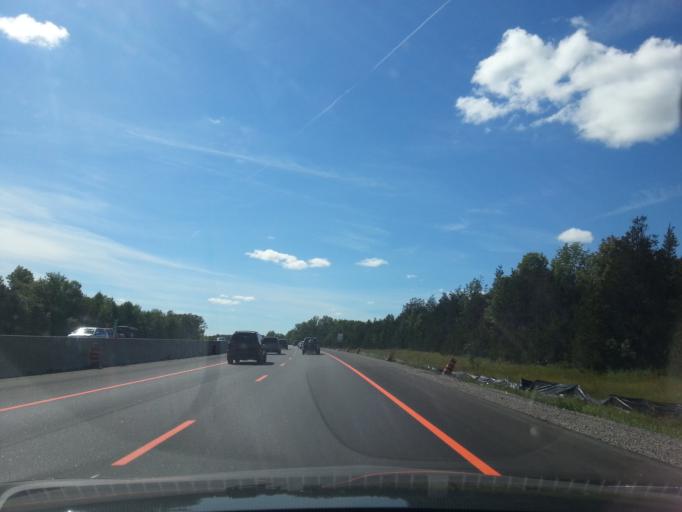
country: CA
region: Ontario
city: Belleville
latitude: 44.2222
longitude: -77.2865
